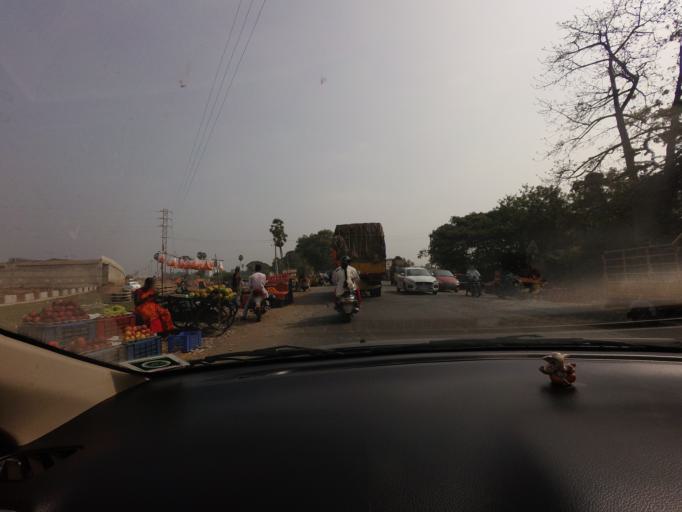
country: IN
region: Andhra Pradesh
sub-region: Krishna
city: Kankipadu
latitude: 16.4418
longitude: 80.7584
